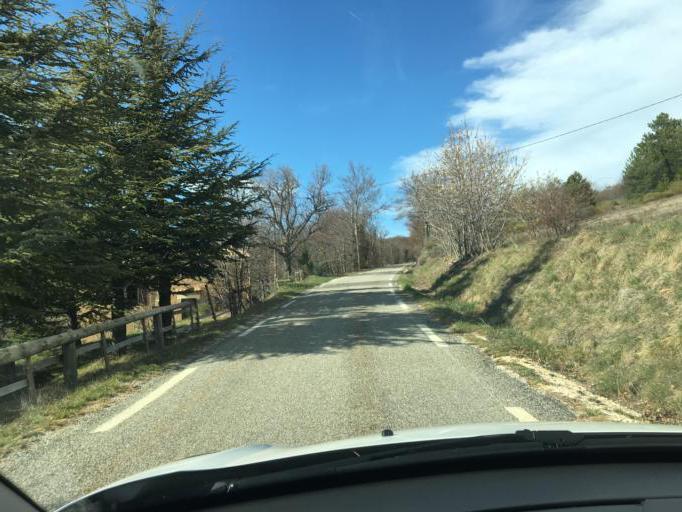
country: FR
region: Provence-Alpes-Cote d'Azur
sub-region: Departement du Vaucluse
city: Saint-Saturnin-les-Apt
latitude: 43.9721
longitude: 5.4617
